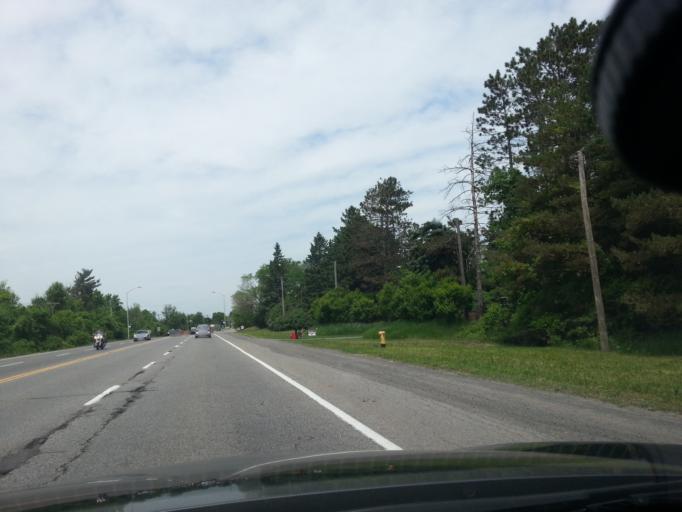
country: CA
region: Ontario
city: Ottawa
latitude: 45.3484
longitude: -75.7023
